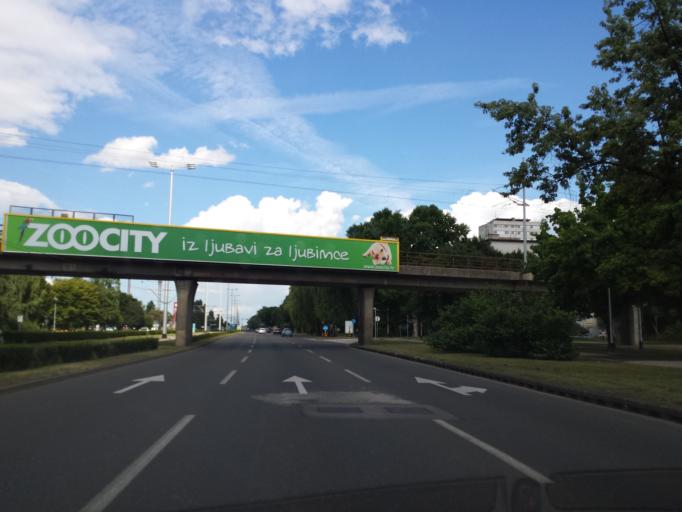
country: HR
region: Grad Zagreb
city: Novi Zagreb
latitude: 45.7769
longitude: 15.9593
